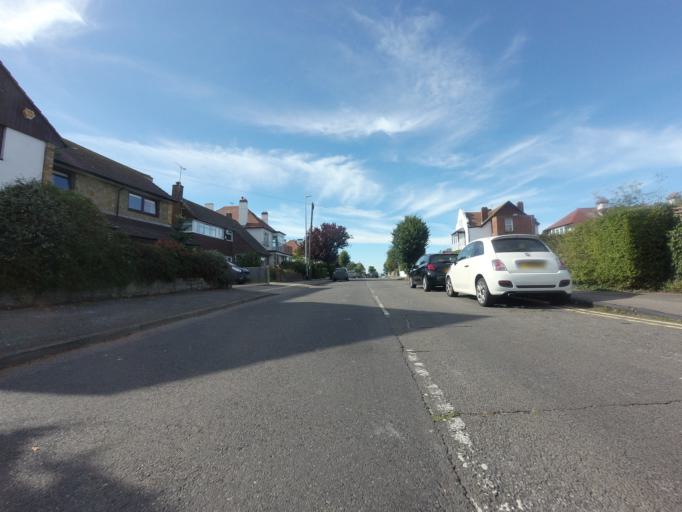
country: GB
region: England
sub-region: Kent
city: Herne Bay
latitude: 51.3703
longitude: 1.1476
